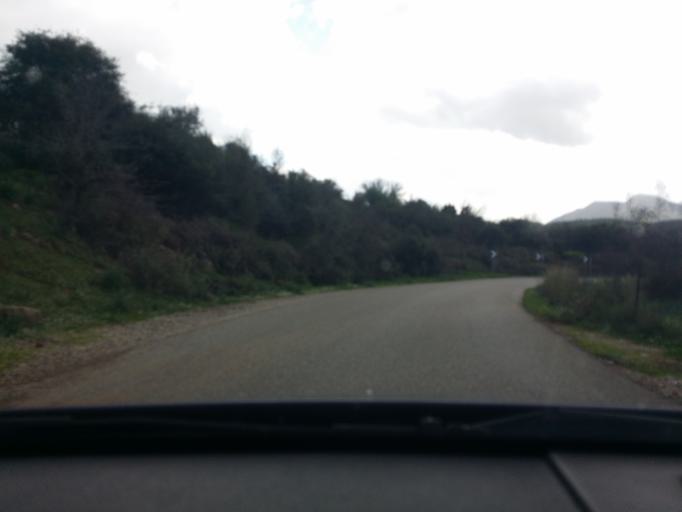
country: GR
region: West Greece
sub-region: Nomos Aitolias kai Akarnanias
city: Fitiai
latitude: 38.6886
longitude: 21.1798
